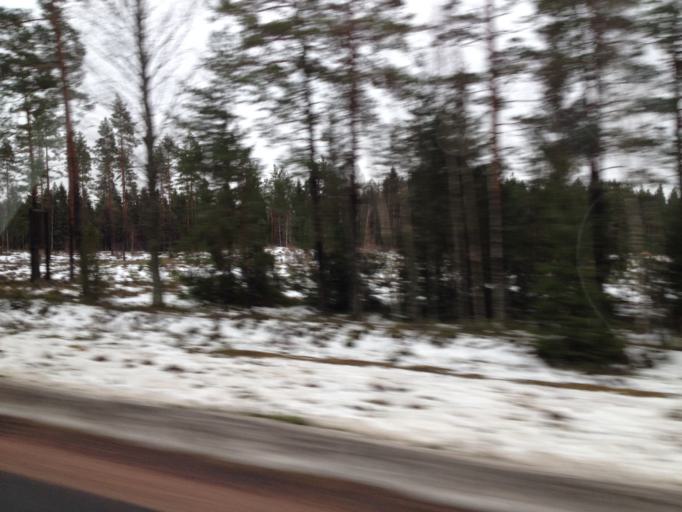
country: FI
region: Uusimaa
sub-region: Raaseporin
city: Karis
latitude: 60.0273
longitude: 23.5851
